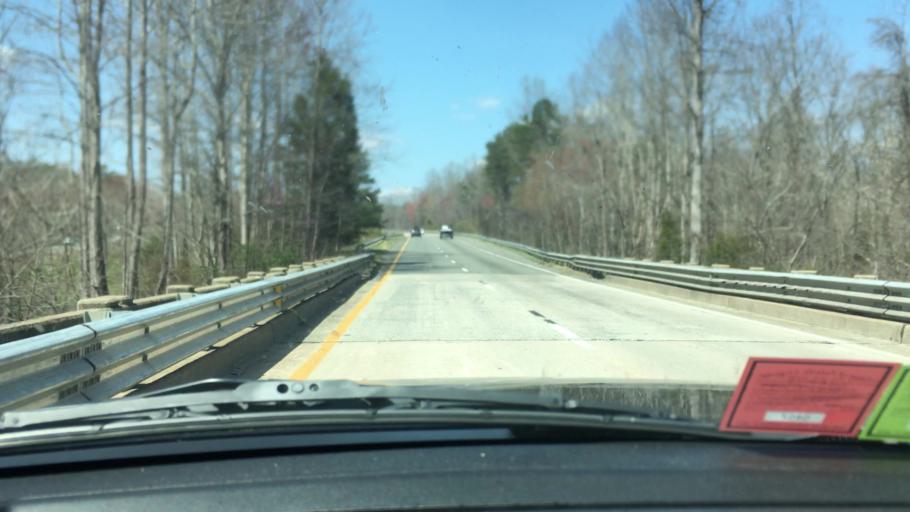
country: US
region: North Carolina
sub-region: Surry County
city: Pilot Mountain
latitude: 36.3973
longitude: -80.4915
